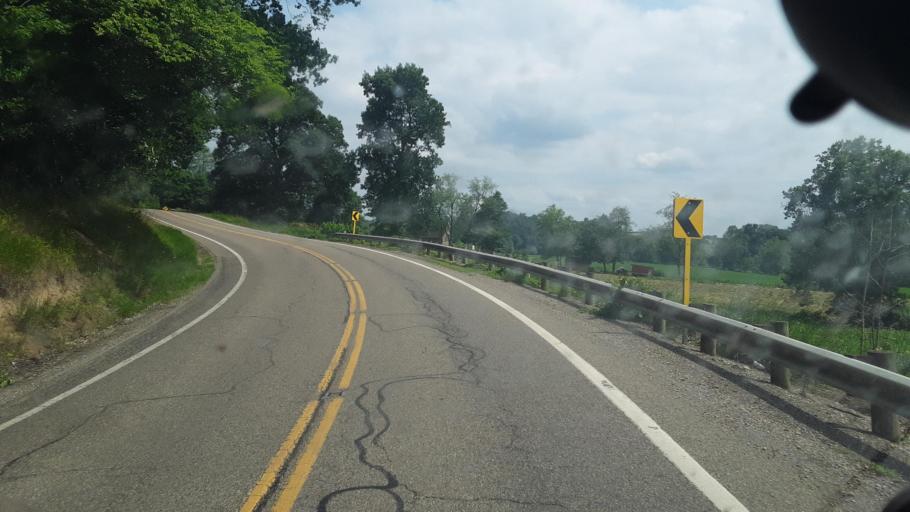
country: US
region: Ohio
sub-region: Coshocton County
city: West Lafayette
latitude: 40.3519
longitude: -81.7350
